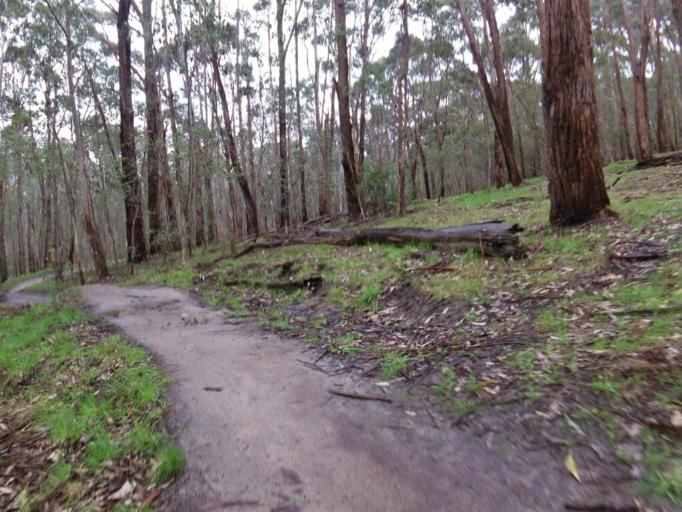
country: AU
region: Victoria
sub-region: Yarra Ranges
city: Lysterfield
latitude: -37.9447
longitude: 145.2824
